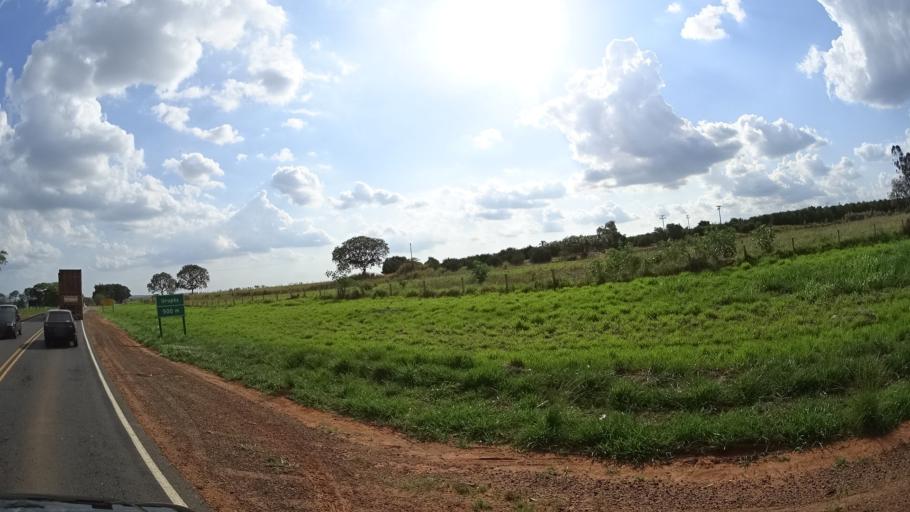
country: BR
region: Sao Paulo
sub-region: Urupes
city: Urupes
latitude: -21.1815
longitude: -49.2931
